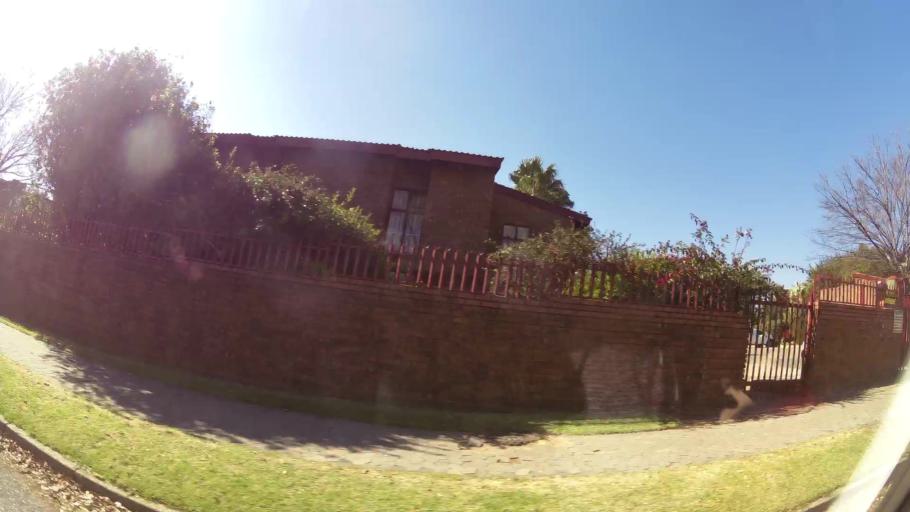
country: ZA
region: Gauteng
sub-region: City of Johannesburg Metropolitan Municipality
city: Johannesburg
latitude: -26.2560
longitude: 28.0678
